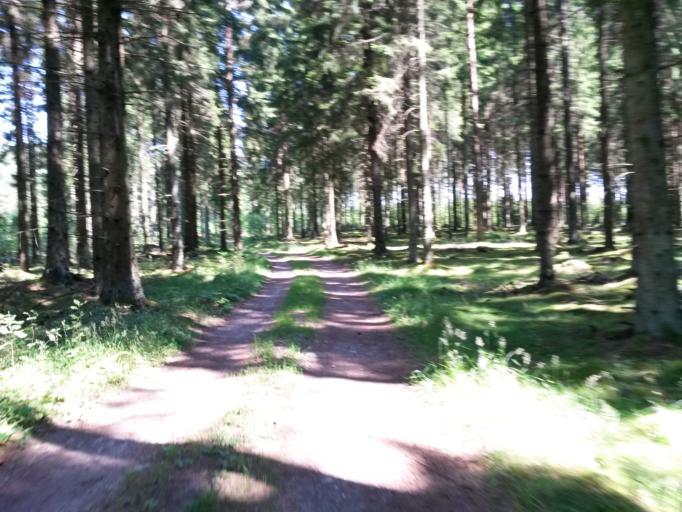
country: SE
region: Vaestra Goetaland
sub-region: Vargarda Kommun
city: Jonstorp
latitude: 57.9847
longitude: 12.6770
